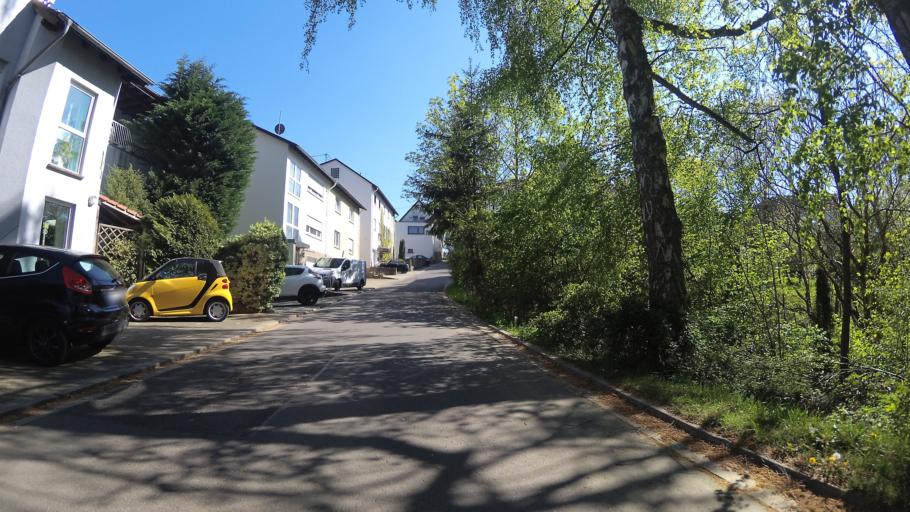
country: DE
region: Saarland
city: Hangard
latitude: 49.3829
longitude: 7.2160
